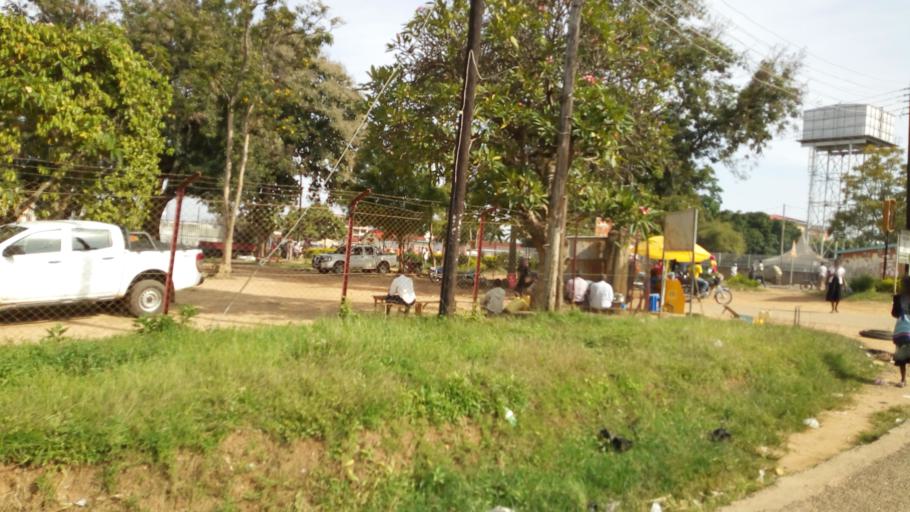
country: UG
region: Northern Region
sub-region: Arua District
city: Arua
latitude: 3.0189
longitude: 30.9119
